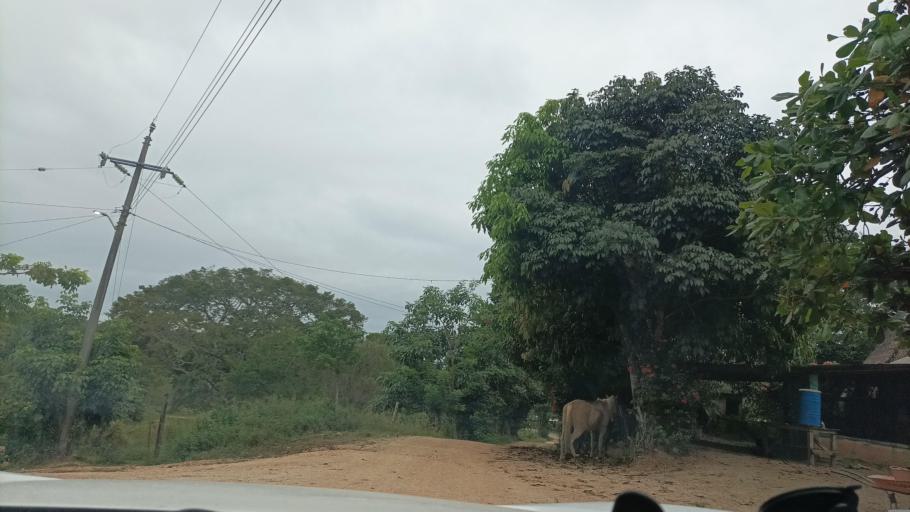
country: MX
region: Veracruz
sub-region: Uxpanapa
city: Poblado Cinco
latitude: 17.4852
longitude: -94.5742
